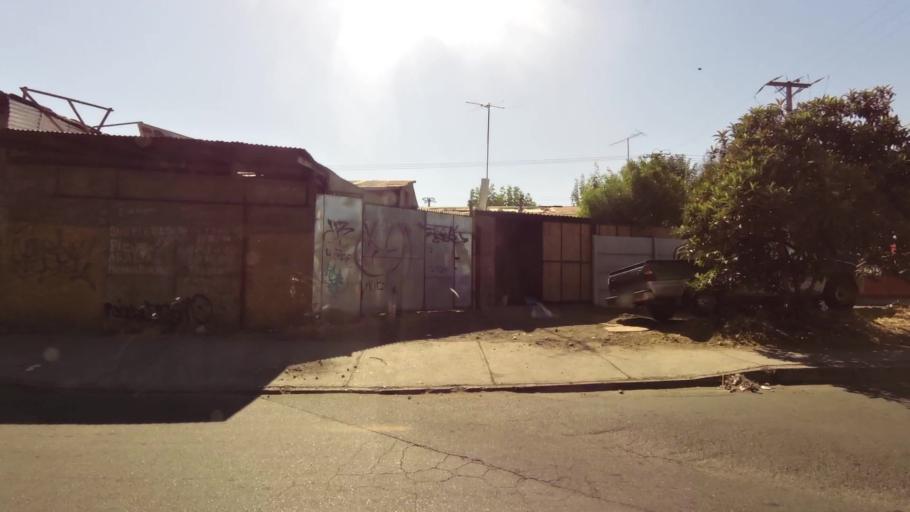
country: CL
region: Maule
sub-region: Provincia de Curico
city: Curico
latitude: -34.9814
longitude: -71.2482
